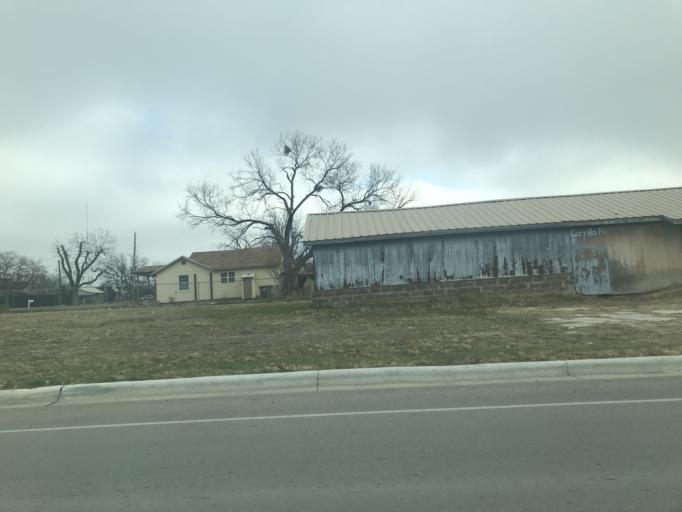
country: US
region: Texas
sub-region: Tom Green County
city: San Angelo
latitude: 31.4822
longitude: -100.4546
